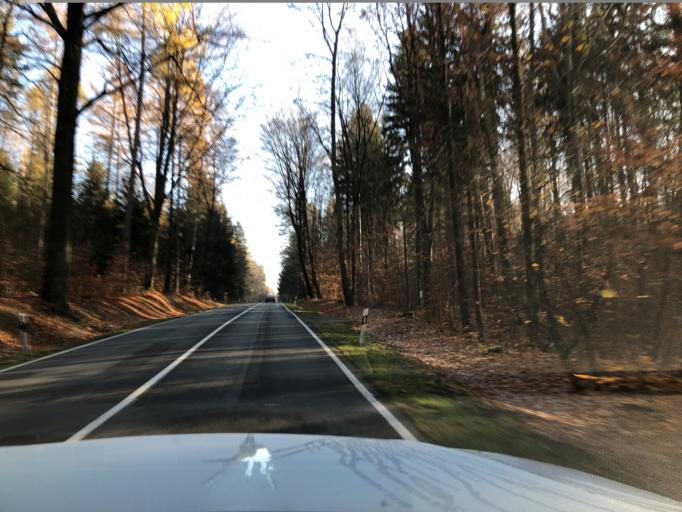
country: DE
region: Saxony
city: Stadt Wehlen
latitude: 50.9878
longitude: 14.0326
